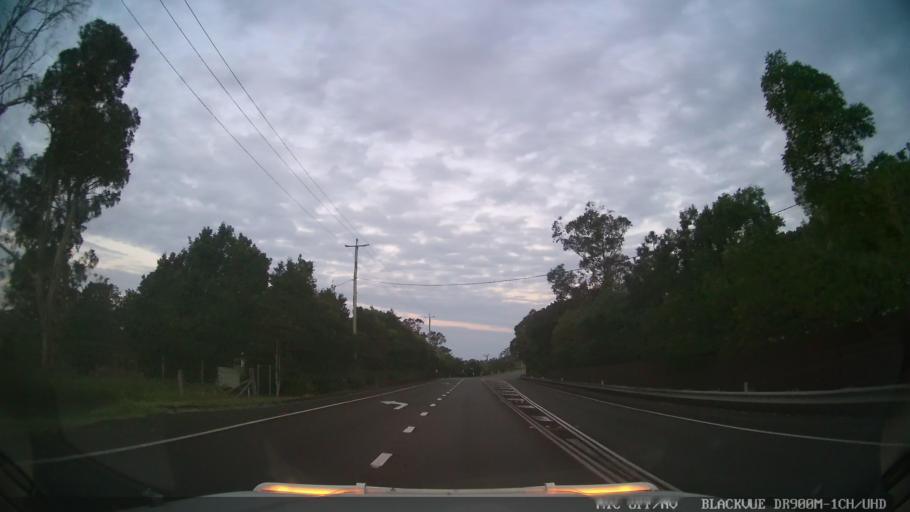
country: AU
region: Queensland
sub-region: Sunshine Coast
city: Nambour
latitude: -26.6175
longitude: 152.8995
